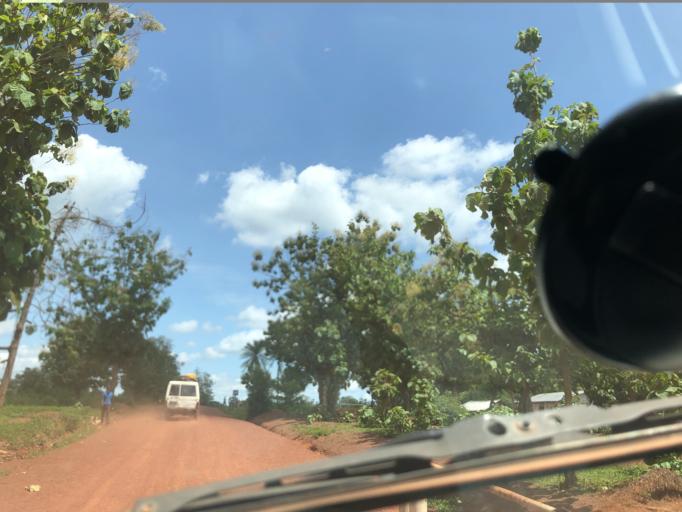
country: CD
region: Equateur
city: Libenge
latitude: 3.7171
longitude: 18.7701
